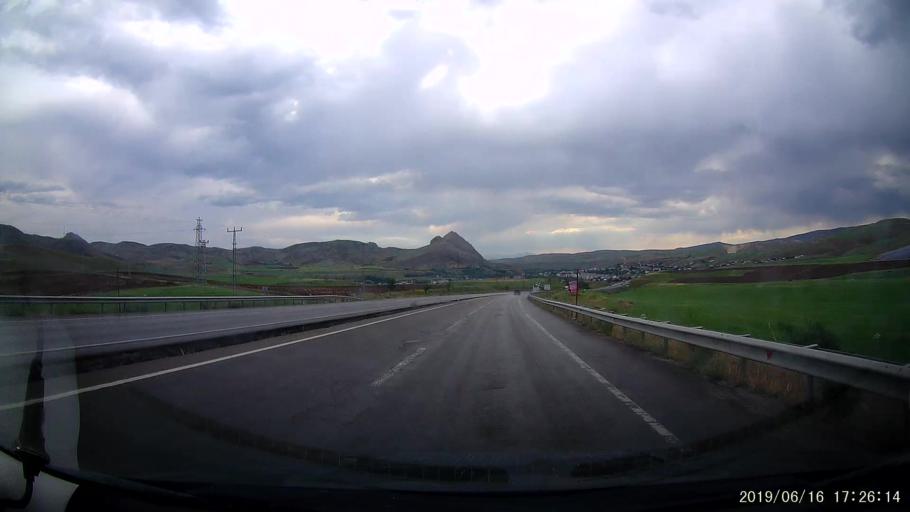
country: TR
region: Erzincan
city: Tercan
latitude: 39.7665
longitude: 40.4170
